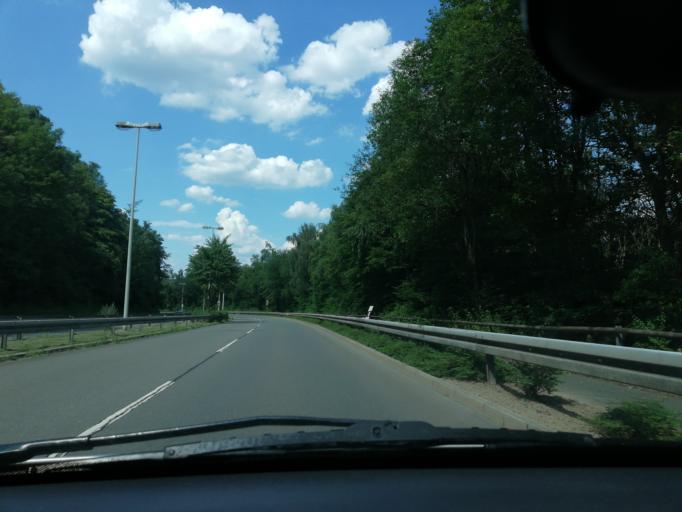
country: DE
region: North Rhine-Westphalia
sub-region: Regierungsbezirk Dusseldorf
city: Wuppertal
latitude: 51.2466
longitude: 7.1636
